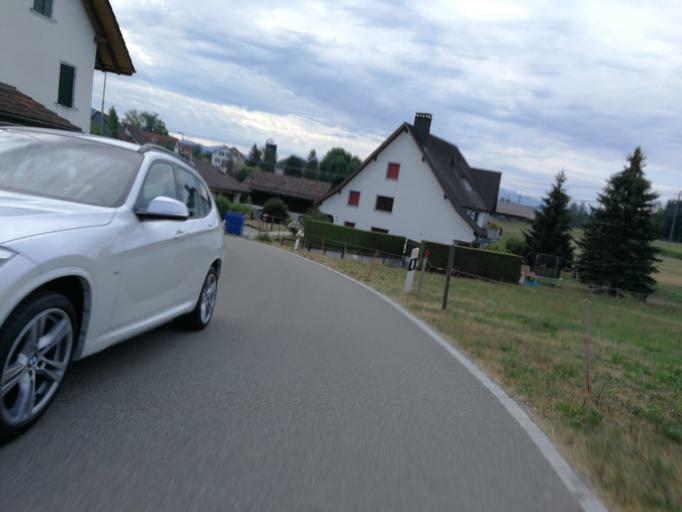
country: CH
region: Zurich
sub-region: Bezirk Hinwil
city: Wetzikon / Robenhausen
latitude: 47.3280
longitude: 8.7721
